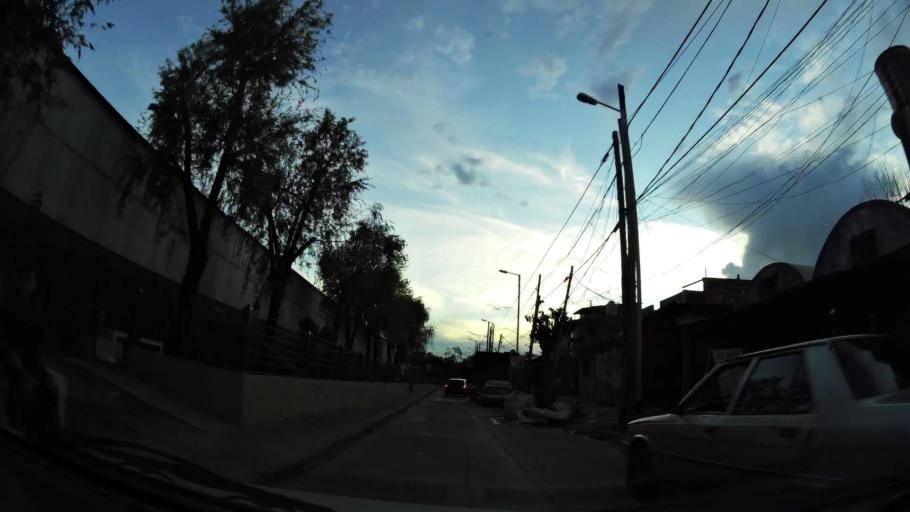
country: AR
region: Buenos Aires
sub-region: Partido de Avellaneda
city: Avellaneda
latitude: -34.6845
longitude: -58.3326
